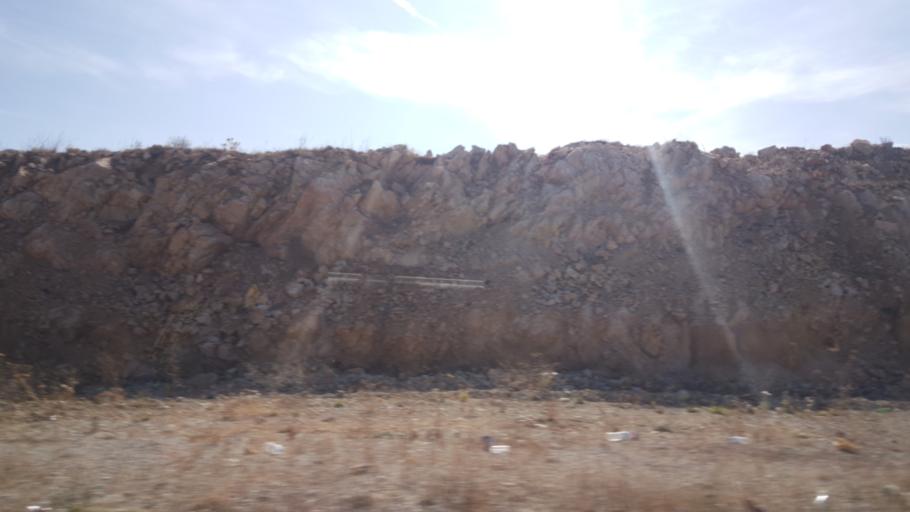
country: TR
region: Ankara
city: Haymana
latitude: 39.4291
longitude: 32.5483
